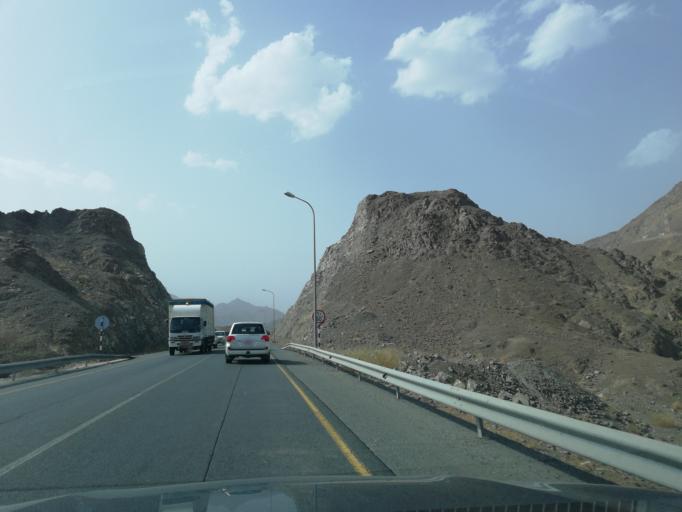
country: OM
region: Muhafazat ad Dakhiliyah
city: Sufalat Sama'il
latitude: 23.1957
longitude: 58.0854
